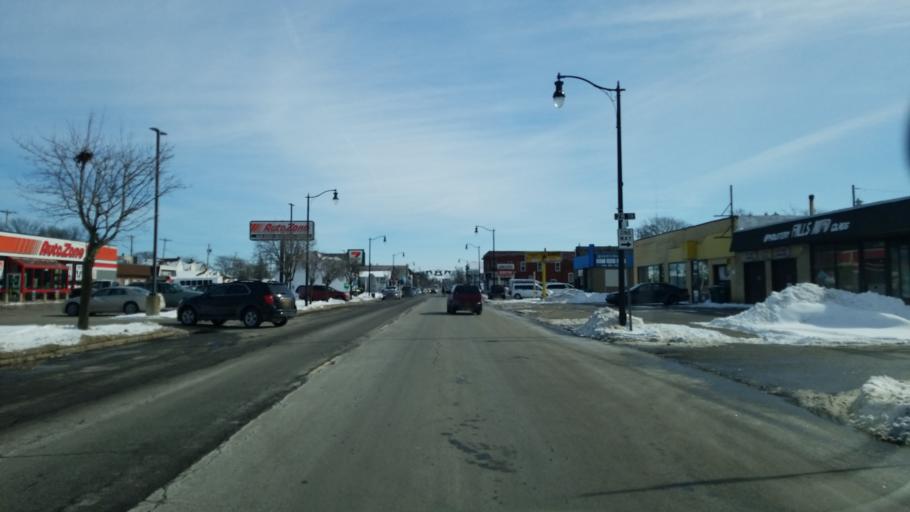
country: US
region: New York
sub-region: Niagara County
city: Niagara Falls
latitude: 43.0951
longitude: -79.0284
